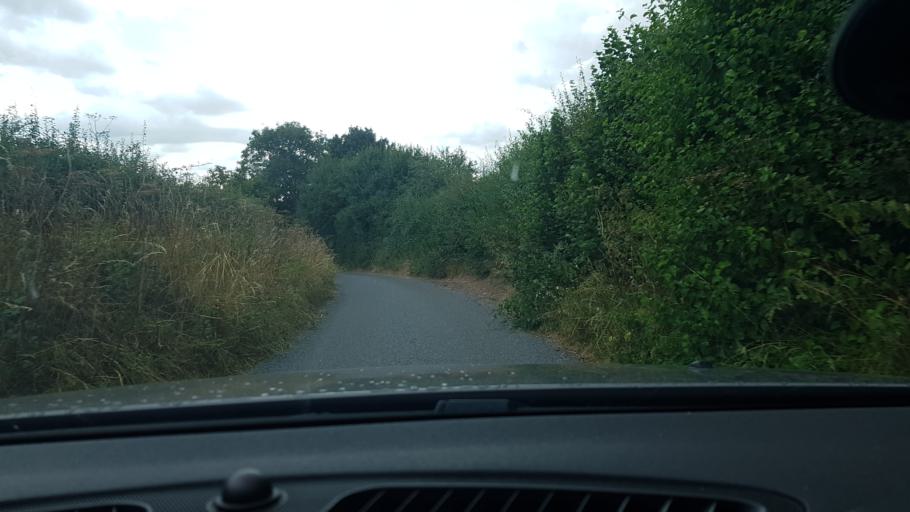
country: GB
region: England
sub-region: West Berkshire
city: Wickham
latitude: 51.4346
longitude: -1.4386
